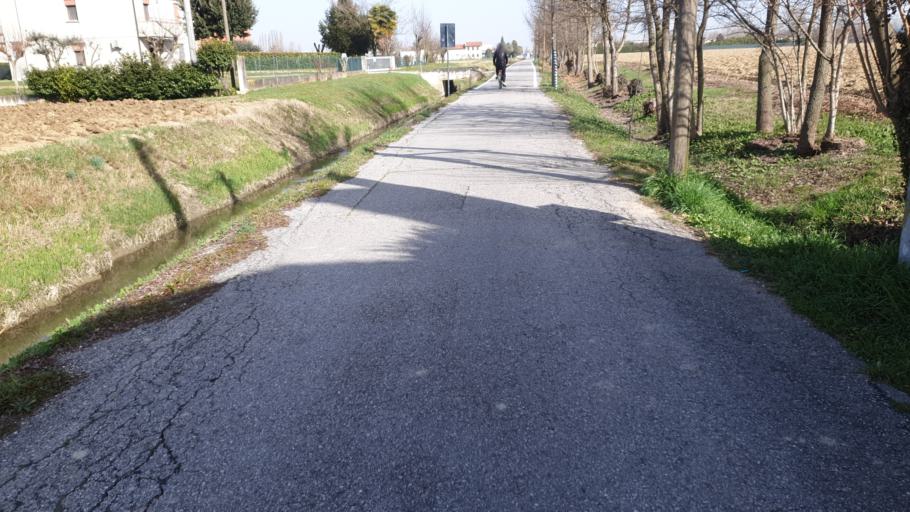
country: IT
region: Veneto
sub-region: Provincia di Padova
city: Mejaniga
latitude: 45.4721
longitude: 11.9148
